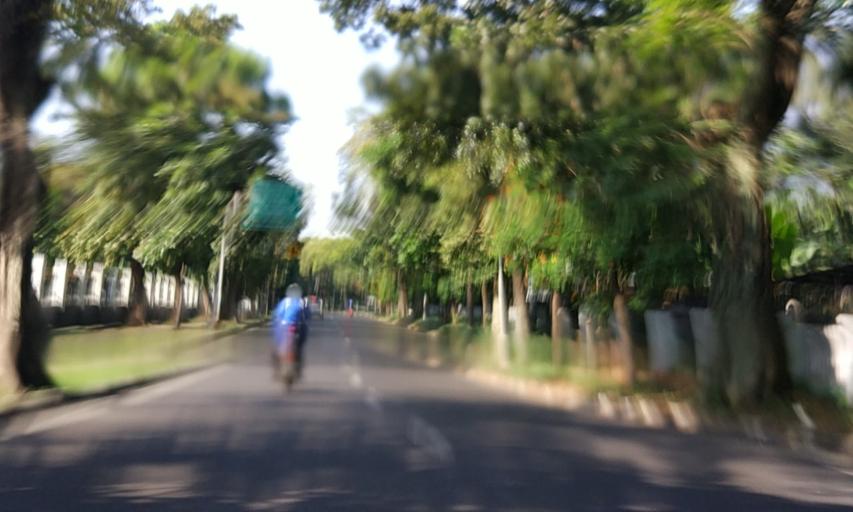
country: ID
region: West Java
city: Bandung
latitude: -6.9111
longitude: 107.6140
